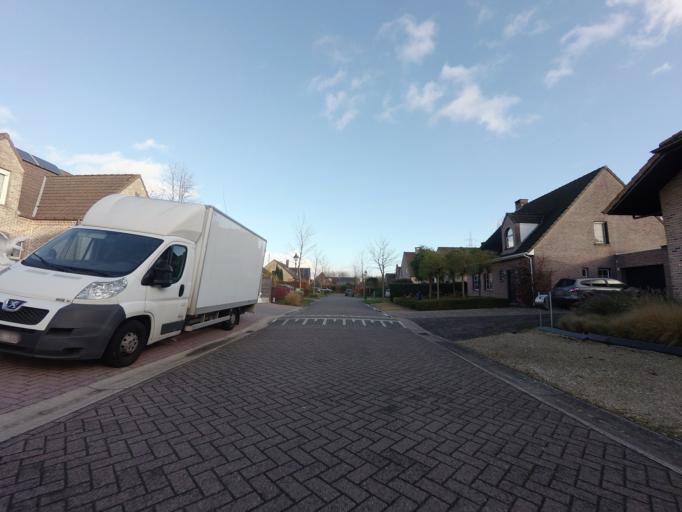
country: BE
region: Flanders
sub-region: Provincie Antwerpen
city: Niel
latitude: 51.1169
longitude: 4.3273
